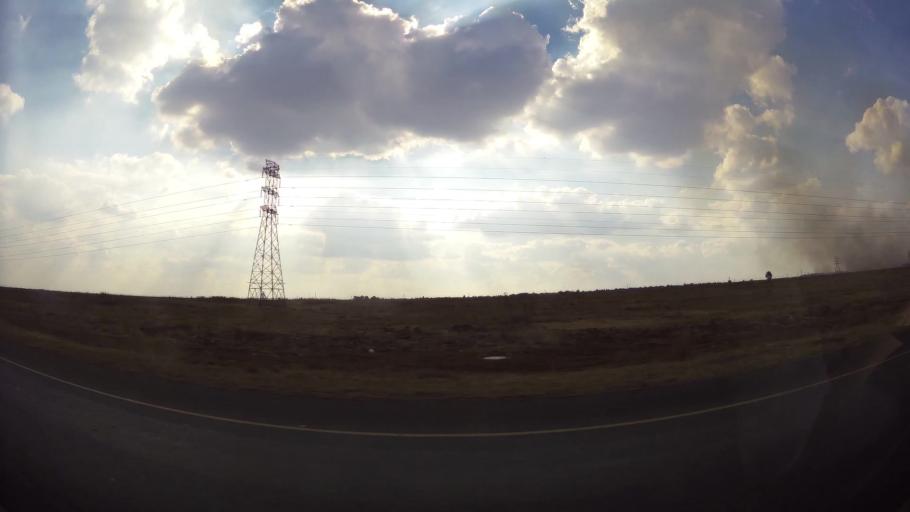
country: ZA
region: Gauteng
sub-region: Ekurhuleni Metropolitan Municipality
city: Boksburg
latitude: -26.2718
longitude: 28.2819
